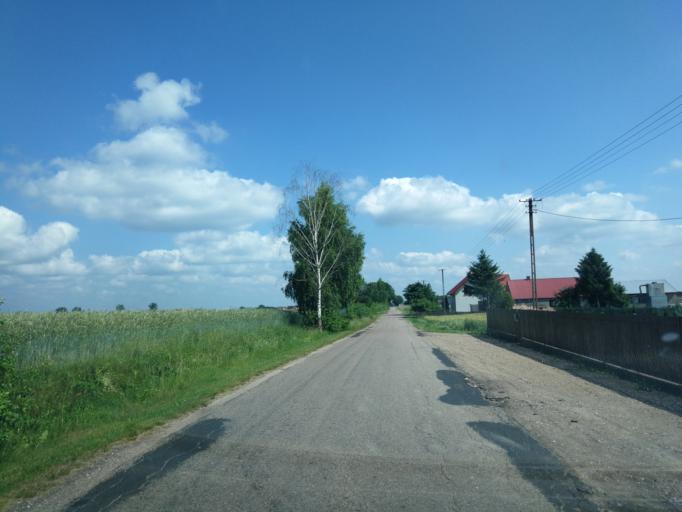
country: PL
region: Warmian-Masurian Voivodeship
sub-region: Powiat dzialdowski
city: Lidzbark
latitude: 53.3147
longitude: 19.8526
